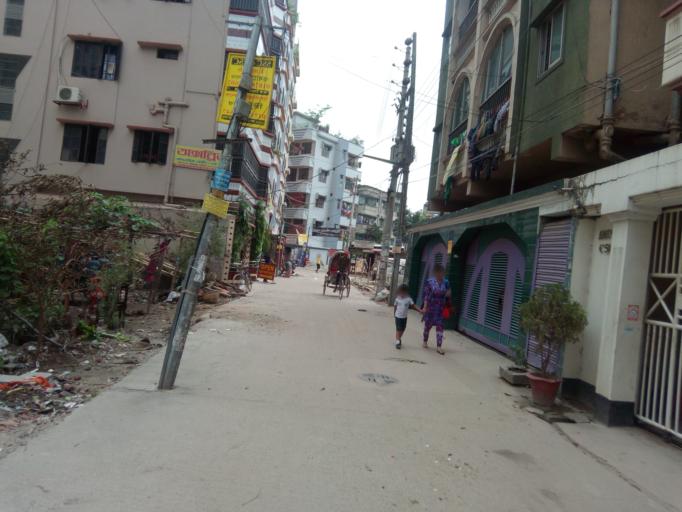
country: BD
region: Dhaka
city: Paltan
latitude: 23.7644
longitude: 90.4142
